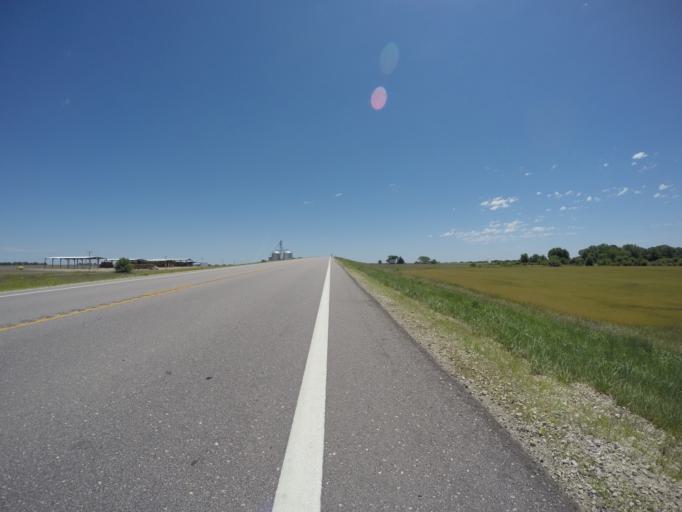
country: US
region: Kansas
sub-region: Republic County
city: Belleville
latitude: 39.8124
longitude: -97.7180
